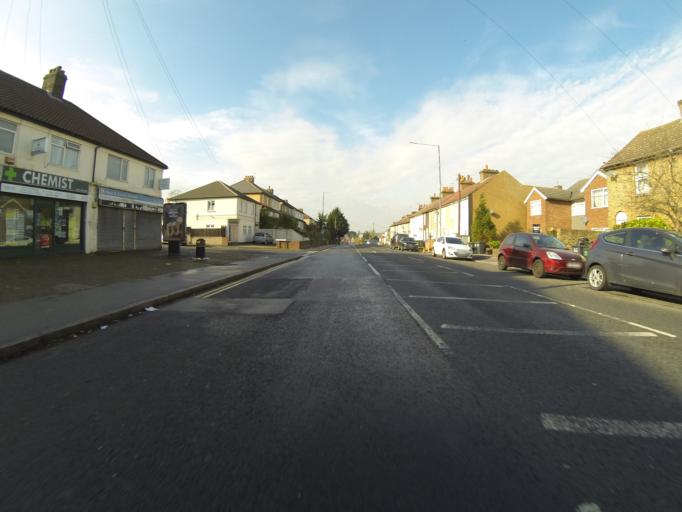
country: GB
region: England
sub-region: Kent
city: Dartford
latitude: 51.4475
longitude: 0.1982
